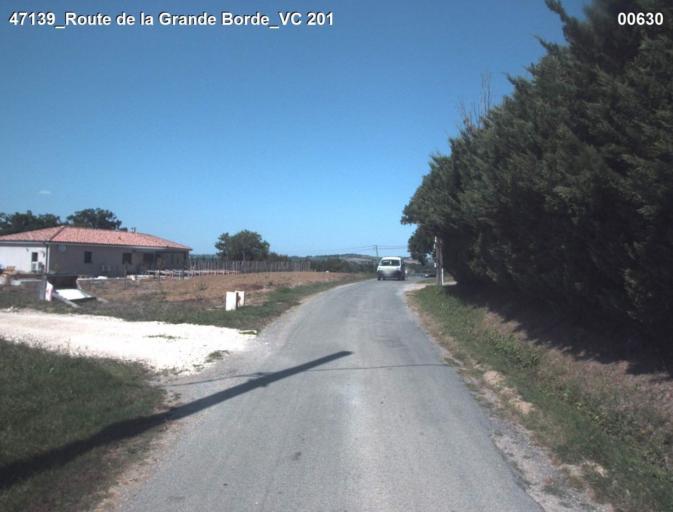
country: FR
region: Aquitaine
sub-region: Departement du Lot-et-Garonne
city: Nerac
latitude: 44.0679
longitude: 0.3927
